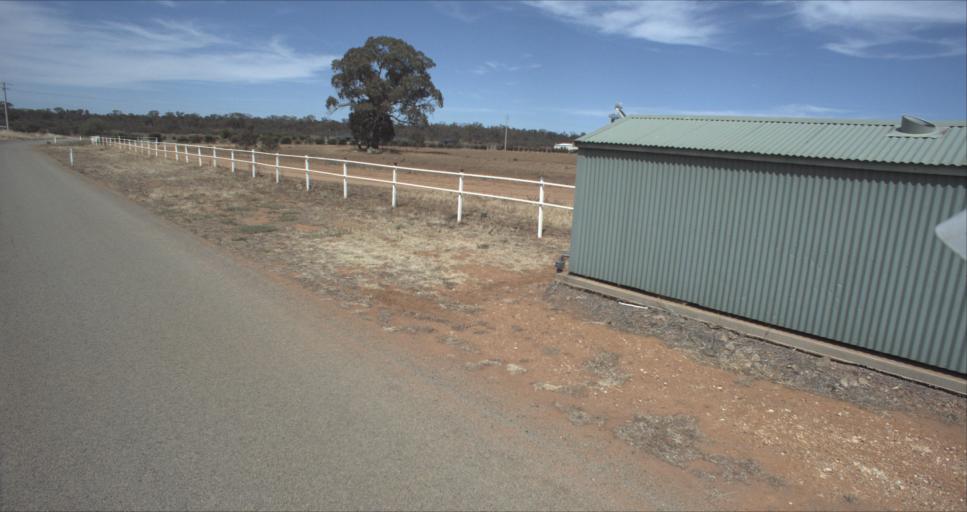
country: AU
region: New South Wales
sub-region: Leeton
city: Leeton
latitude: -34.5765
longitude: 146.4555
